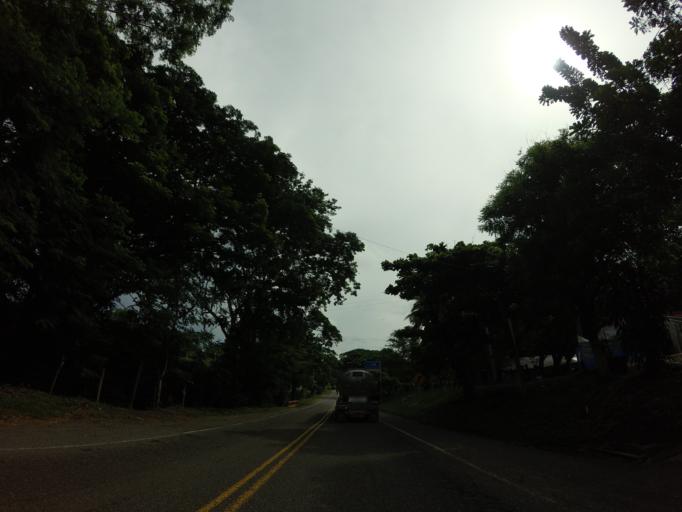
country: CO
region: Caldas
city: La Dorada
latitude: 5.4373
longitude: -74.6794
